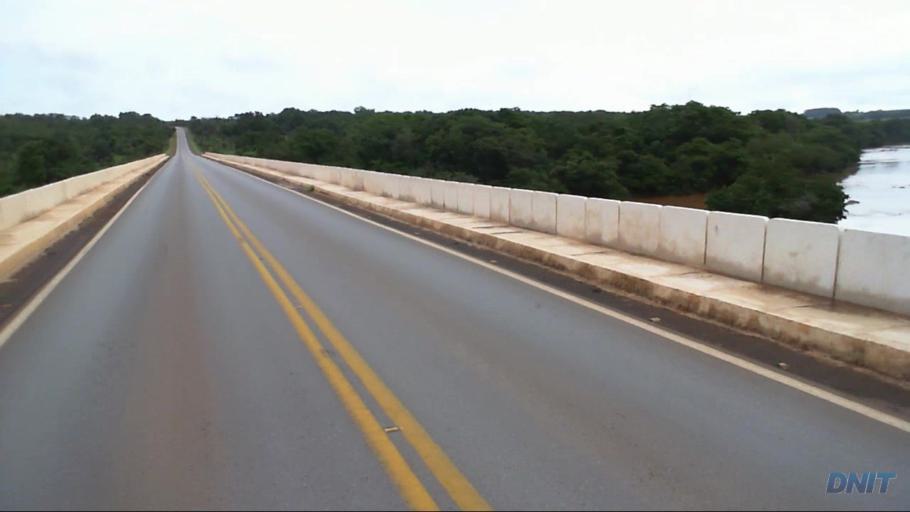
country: BR
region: Goias
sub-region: Uruacu
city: Uruacu
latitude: -14.7489
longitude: -49.0750
